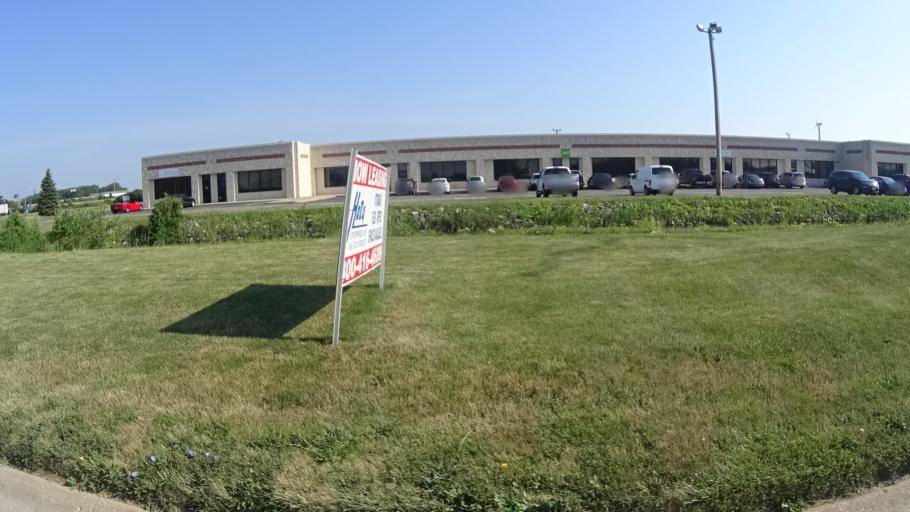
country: US
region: Ohio
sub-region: Erie County
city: Huron
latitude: 41.4013
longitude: -82.5882
